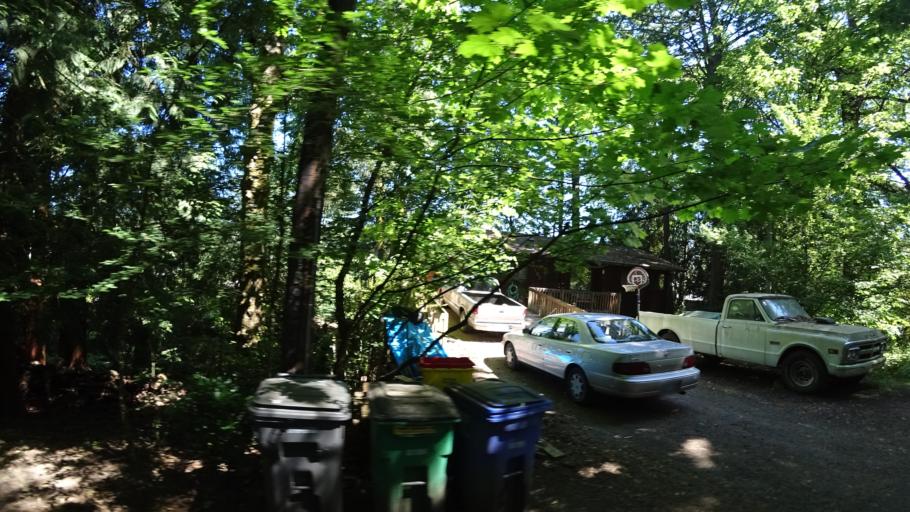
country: US
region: Oregon
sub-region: Washington County
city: Raleigh Hills
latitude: 45.4857
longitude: -122.7304
